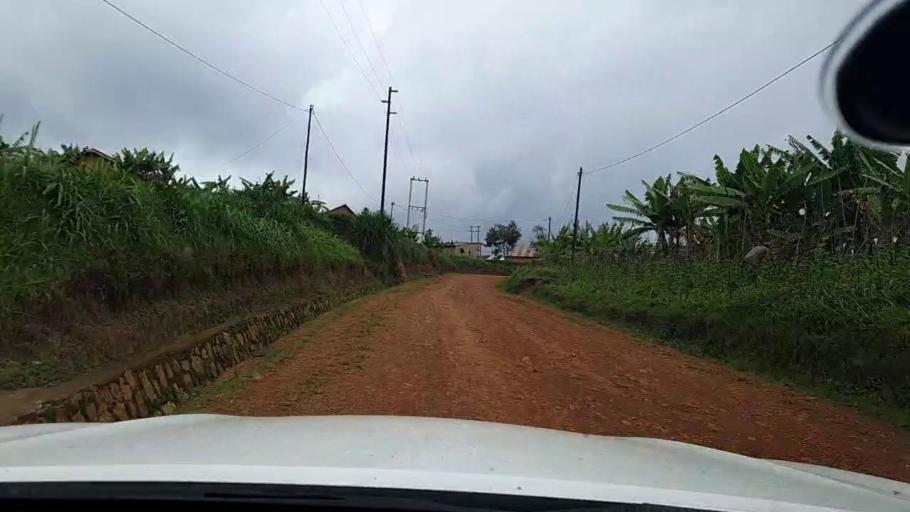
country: RW
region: Western Province
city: Kibuye
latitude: -2.1754
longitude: 29.4430
